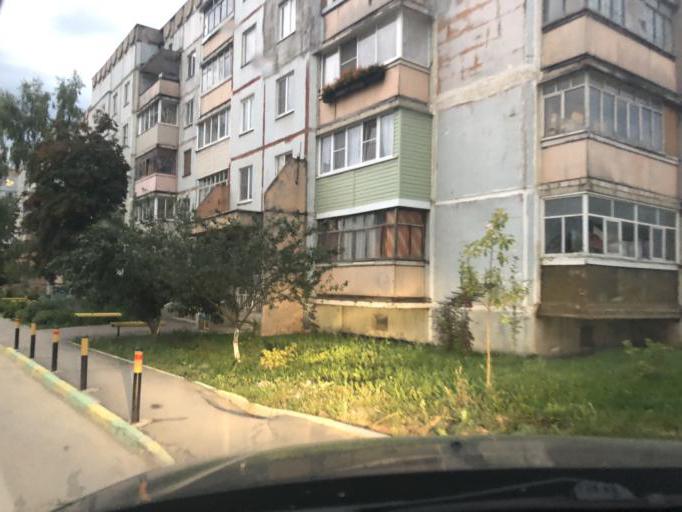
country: RU
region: Tula
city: Gorelki
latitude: 54.2281
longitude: 37.6147
